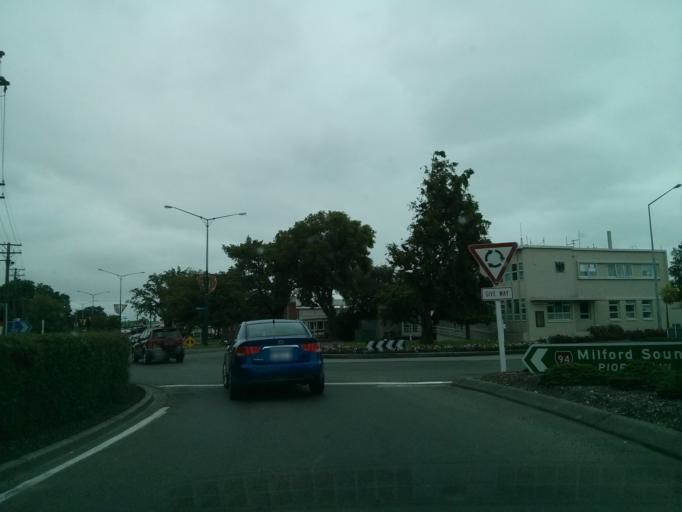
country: NZ
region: Southland
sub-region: Gore District
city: Gore
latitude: -46.0994
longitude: 168.9454
